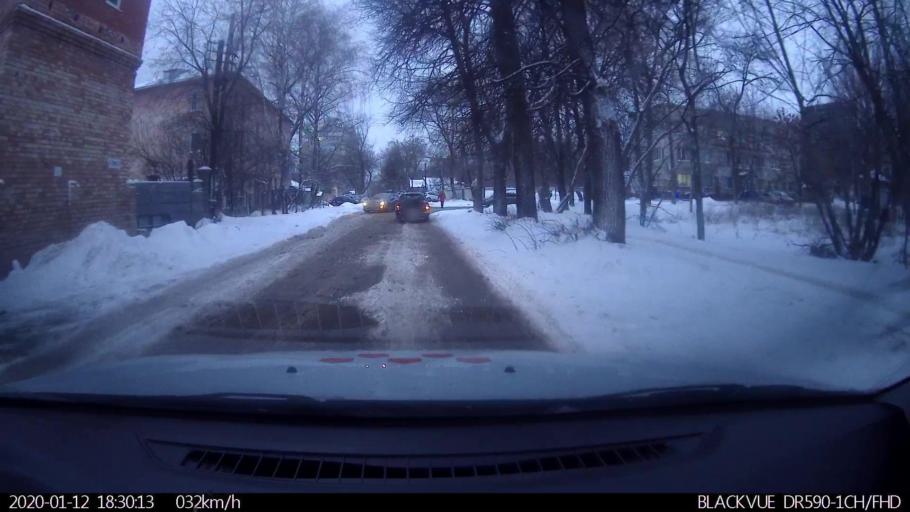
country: RU
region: Nizjnij Novgorod
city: Nizhniy Novgorod
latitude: 56.3199
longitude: 44.0377
